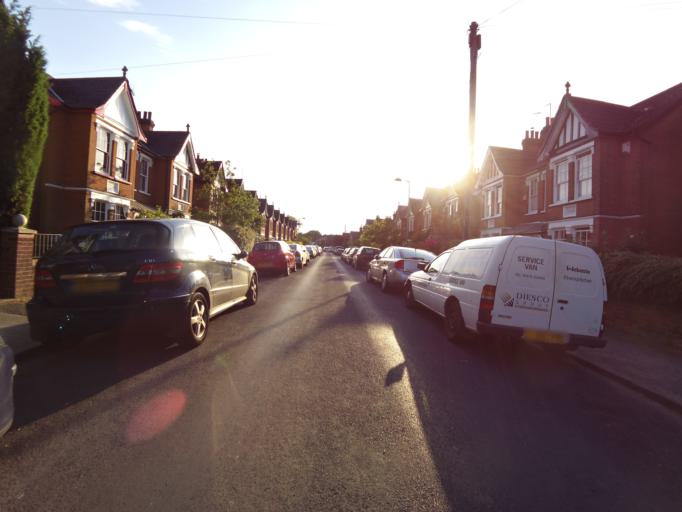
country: GB
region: England
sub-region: Suffolk
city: Ipswich
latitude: 52.0557
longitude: 1.1813
